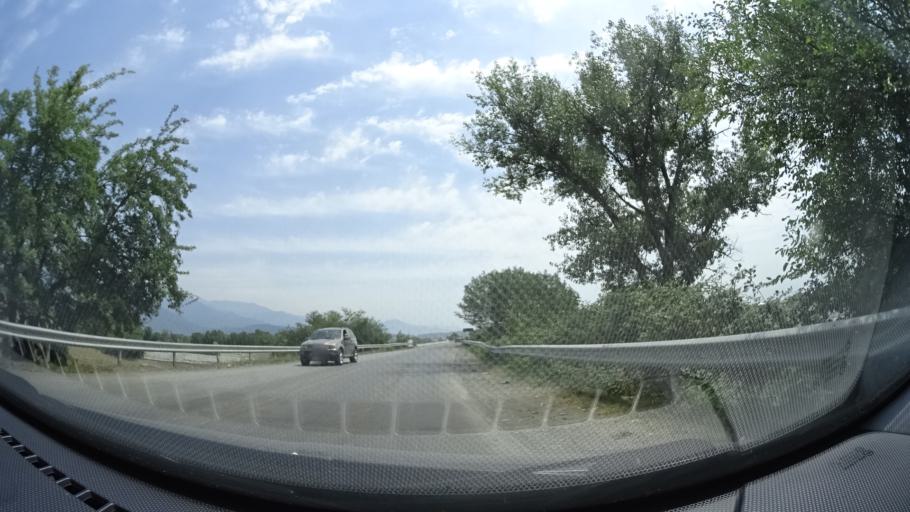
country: GE
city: Bagdadi
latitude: 41.8403
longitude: 46.1034
